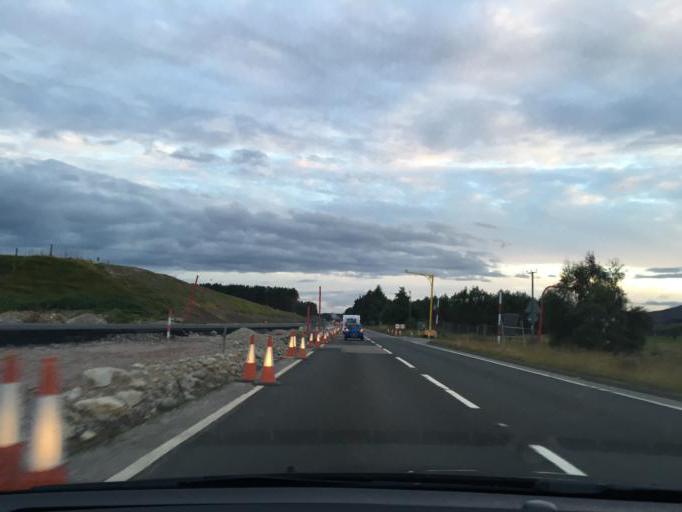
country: GB
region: Scotland
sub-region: Highland
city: Aviemore
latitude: 57.1570
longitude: -3.8984
